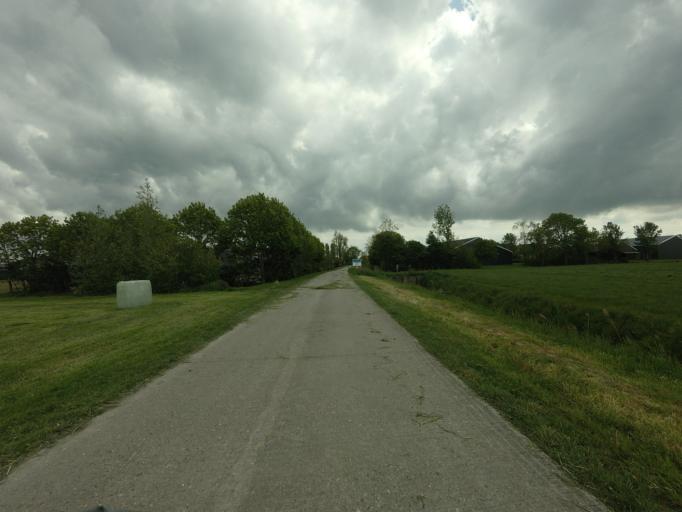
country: NL
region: Friesland
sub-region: Gemeente Littenseradiel
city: Wommels
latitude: 53.1038
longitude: 5.6230
